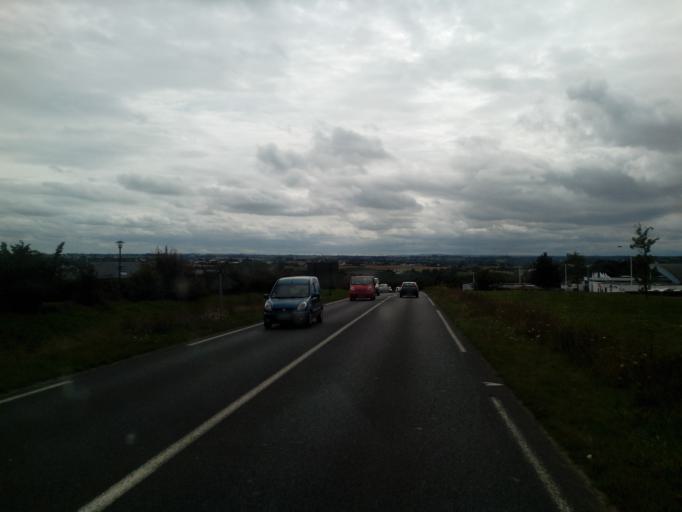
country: FR
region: Brittany
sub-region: Departement des Cotes-d'Armor
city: Binic
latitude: 48.6107
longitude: -2.8320
